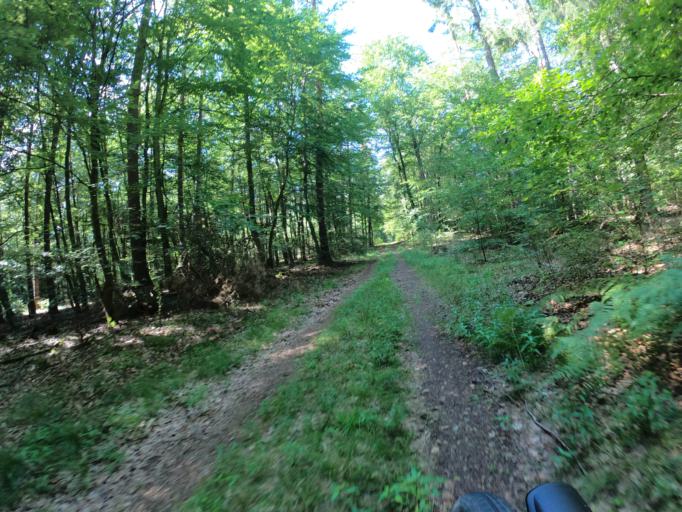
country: DE
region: Hesse
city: Langen
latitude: 49.9922
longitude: 8.6269
